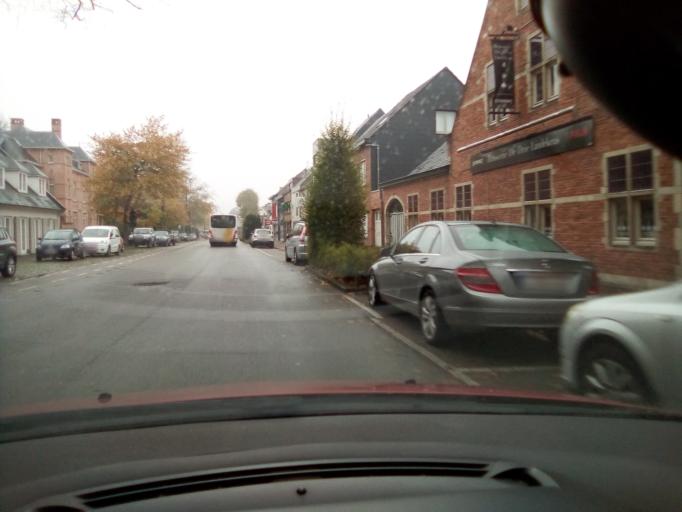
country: BE
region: Flanders
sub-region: Provincie Oost-Vlaanderen
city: Waasmunster
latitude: 51.1462
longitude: 4.0857
